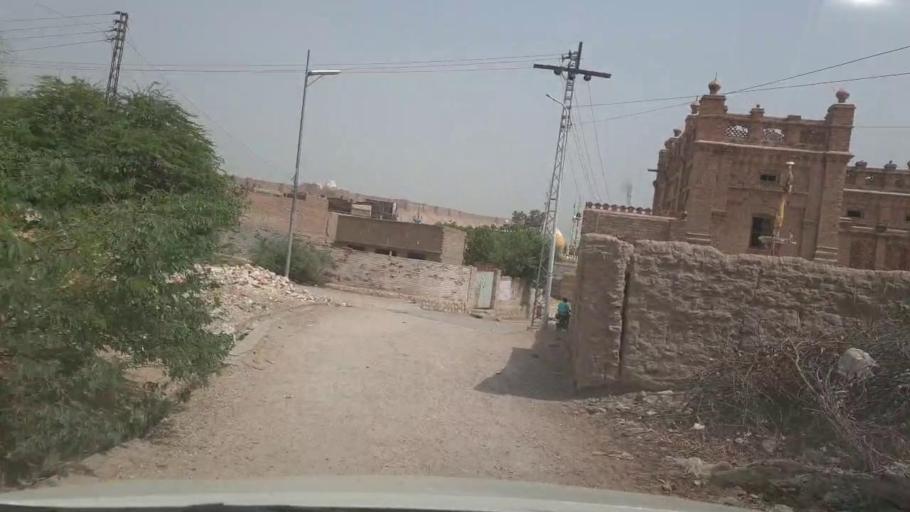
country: PK
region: Sindh
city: Kot Diji
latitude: 27.3388
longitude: 68.7079
